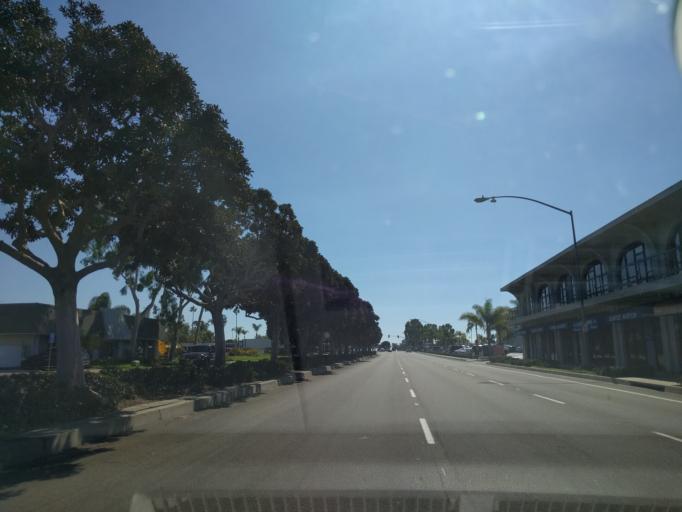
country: US
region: California
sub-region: Orange County
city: Irvine
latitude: 33.6665
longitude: -117.8711
